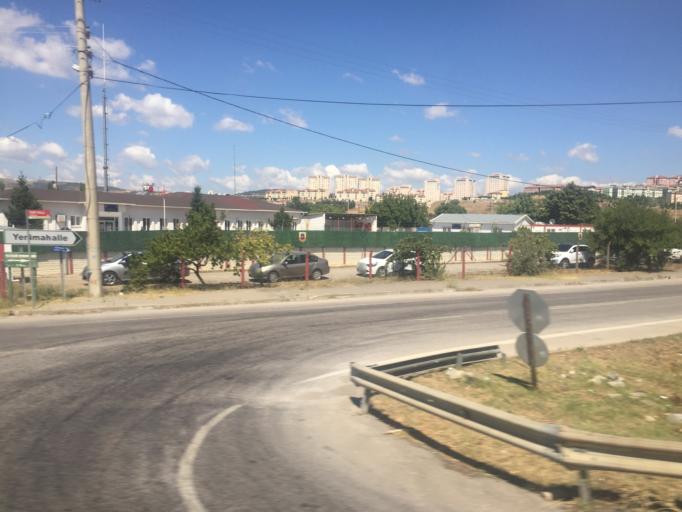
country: TR
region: Balikesir
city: Balikesir
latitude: 39.6876
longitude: 27.9477
